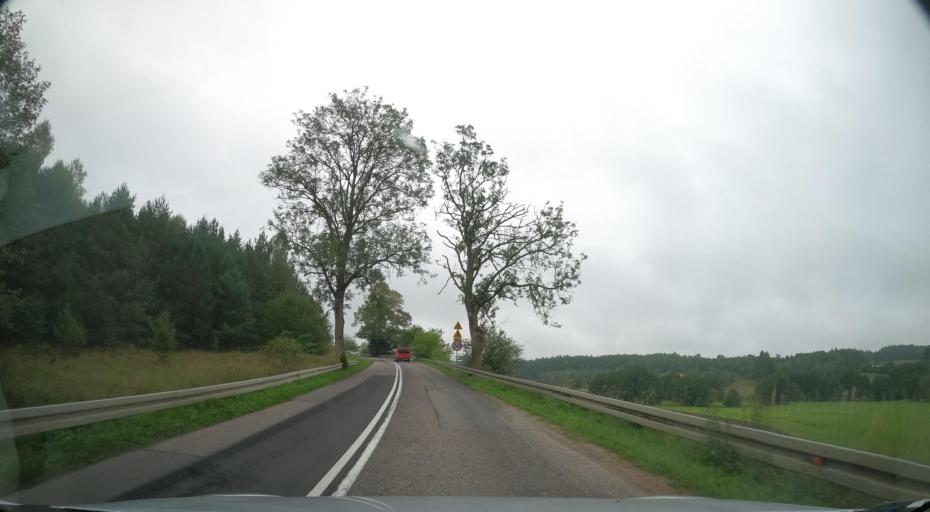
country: PL
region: Pomeranian Voivodeship
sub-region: Powiat wejherowski
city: Linia
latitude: 54.4578
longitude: 18.0024
